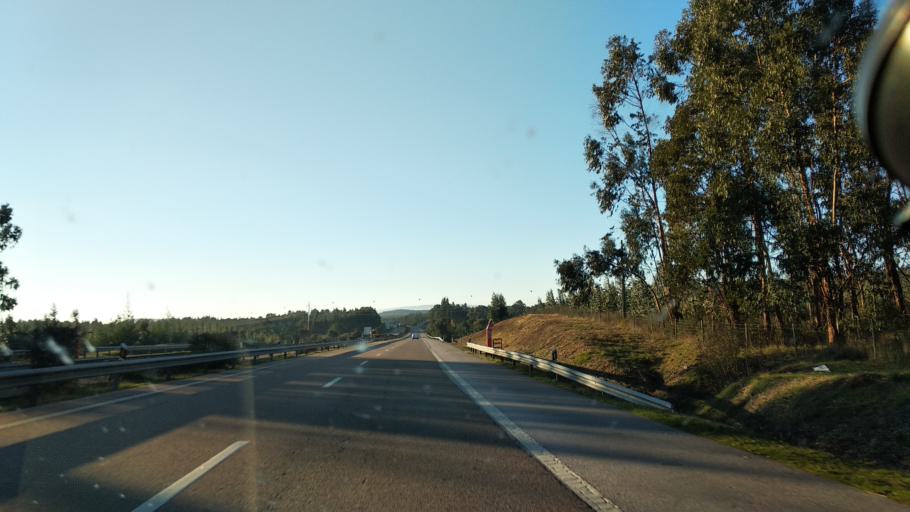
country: PT
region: Santarem
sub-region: Constancia
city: Constancia
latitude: 39.4847
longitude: -8.3729
